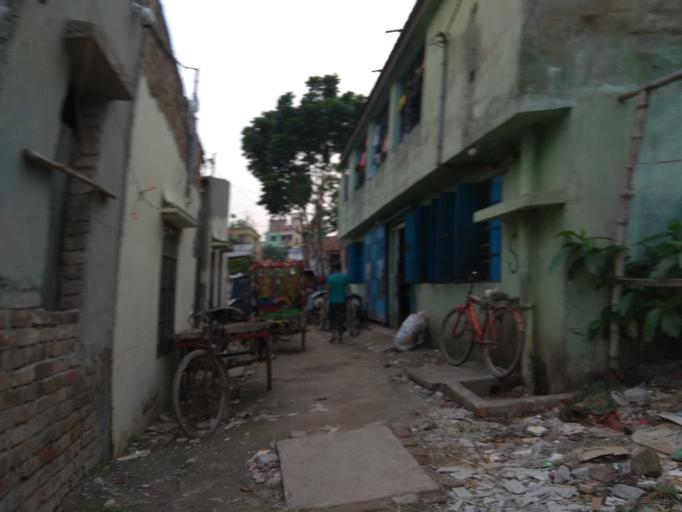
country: BD
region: Dhaka
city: Tungi
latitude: 23.8145
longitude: 90.3819
